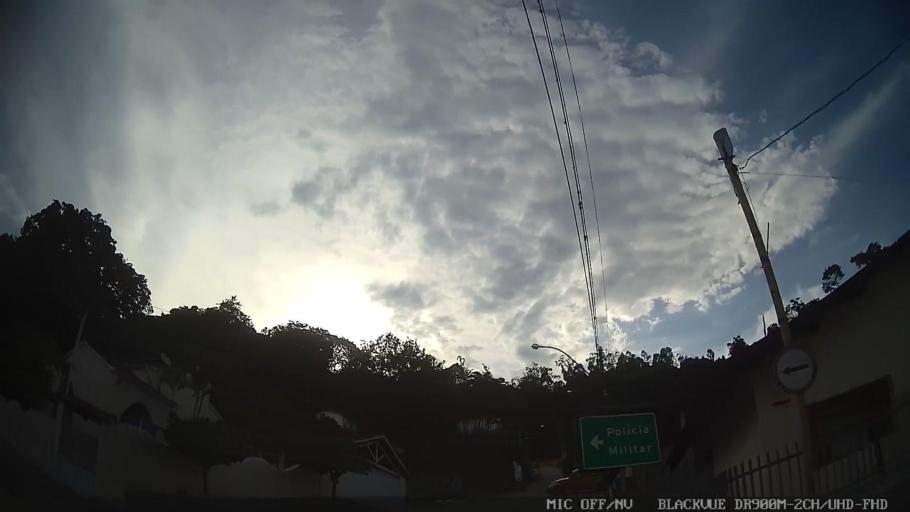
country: BR
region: Sao Paulo
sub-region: Serra Negra
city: Serra Negra
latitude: -22.6828
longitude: -46.6809
